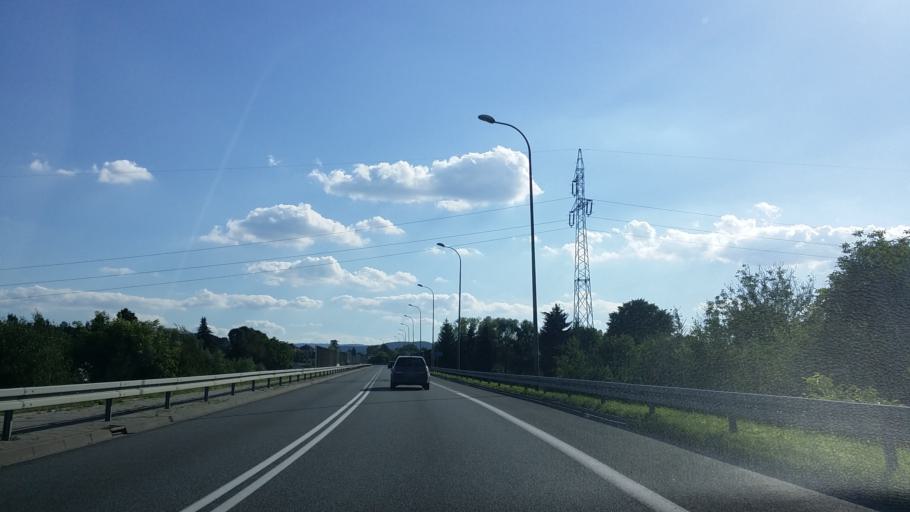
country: PL
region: Lesser Poland Voivodeship
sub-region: Powiat wadowicki
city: Tomice
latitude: 49.8860
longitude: 19.4761
